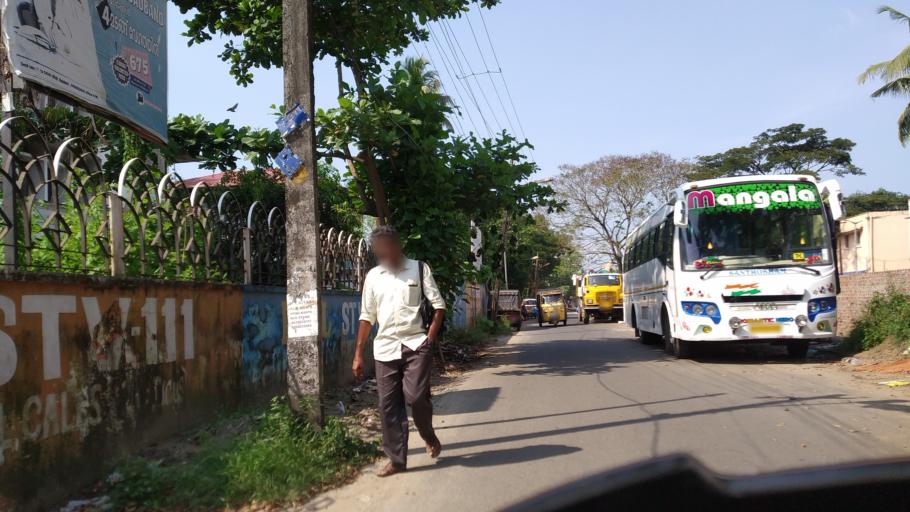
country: IN
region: Kerala
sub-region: Ernakulam
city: Cochin
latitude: 9.9712
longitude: 76.2899
